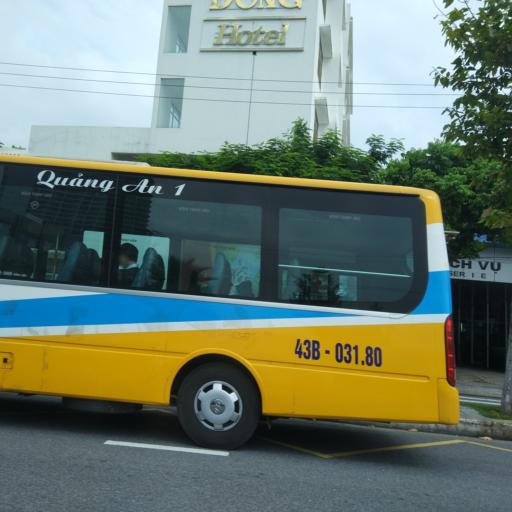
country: VN
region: Da Nang
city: Son Tra
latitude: 16.0710
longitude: 108.2313
